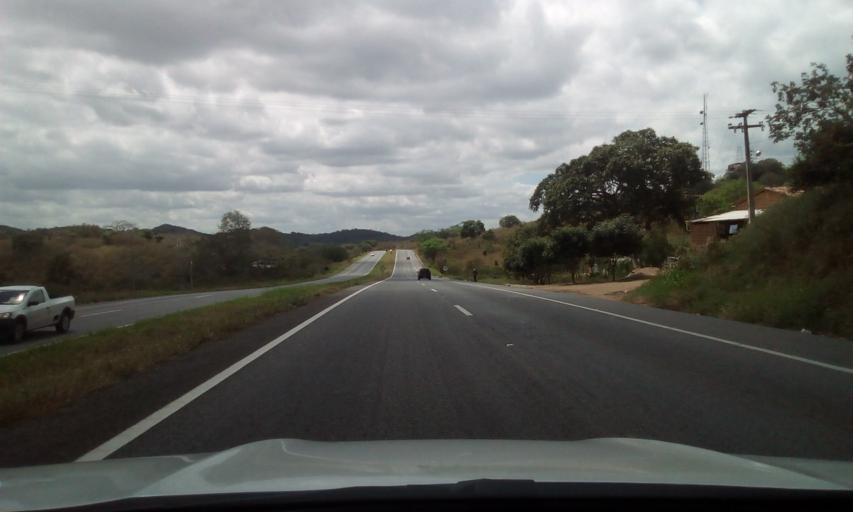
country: BR
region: Paraiba
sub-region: Massaranduba
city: Massaranduba
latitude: -7.2692
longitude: -35.7920
